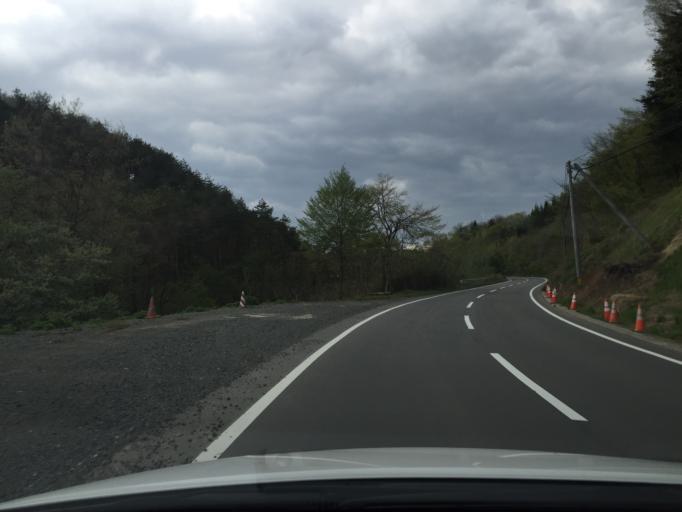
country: JP
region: Fukushima
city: Yanagawamachi-saiwaicho
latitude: 37.7288
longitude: 140.7340
